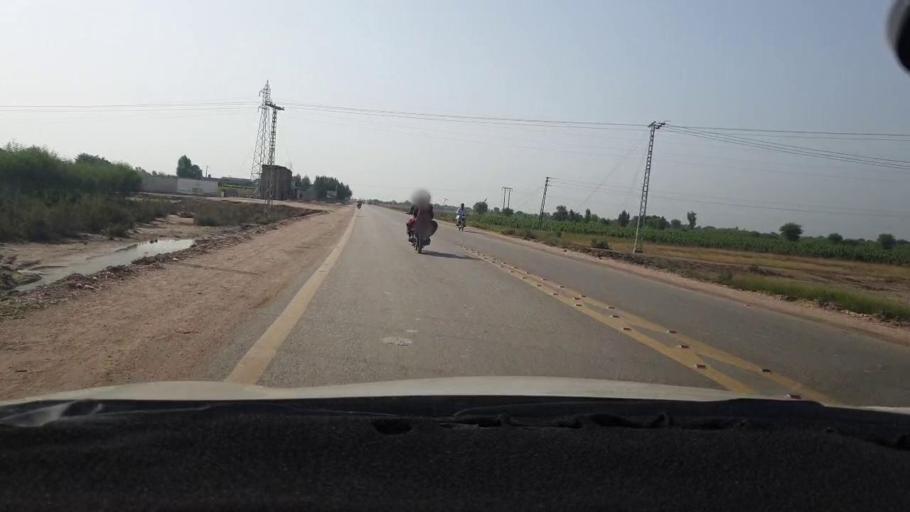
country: PK
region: Sindh
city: Sanghar
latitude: 26.0279
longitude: 68.9539
